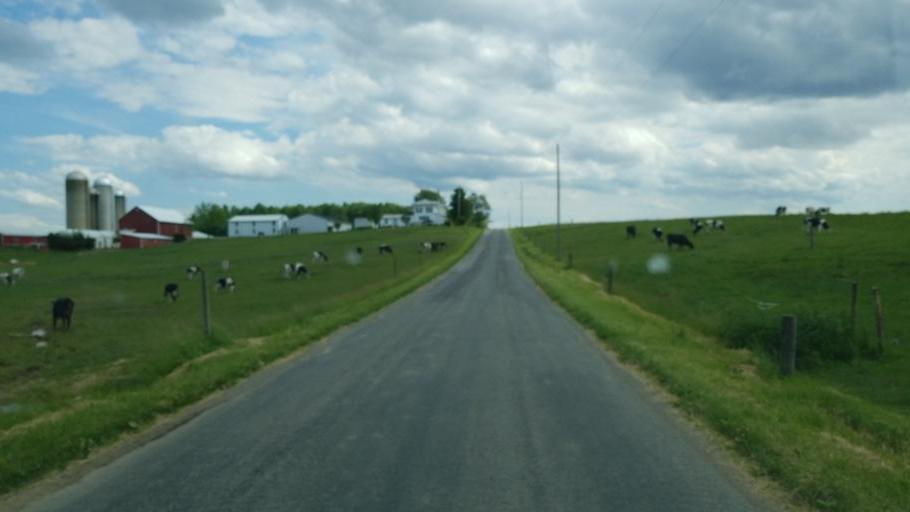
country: US
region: Ohio
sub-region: Huron County
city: Plymouth
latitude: 40.9631
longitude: -82.6392
